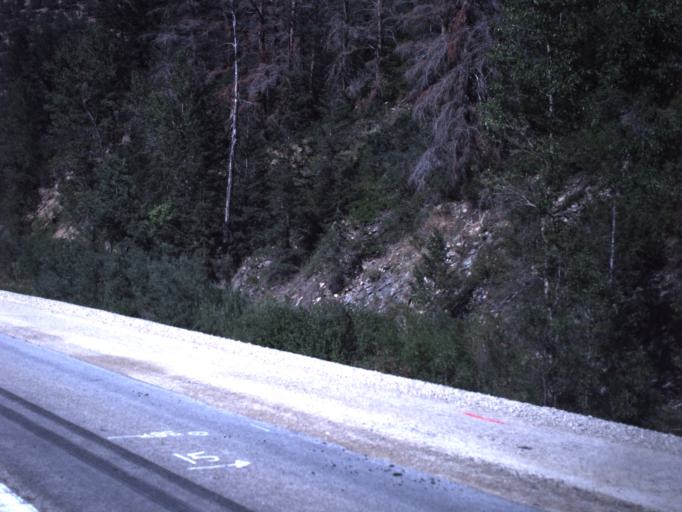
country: US
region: Utah
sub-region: Wasatch County
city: Heber
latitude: 40.3736
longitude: -111.2945
